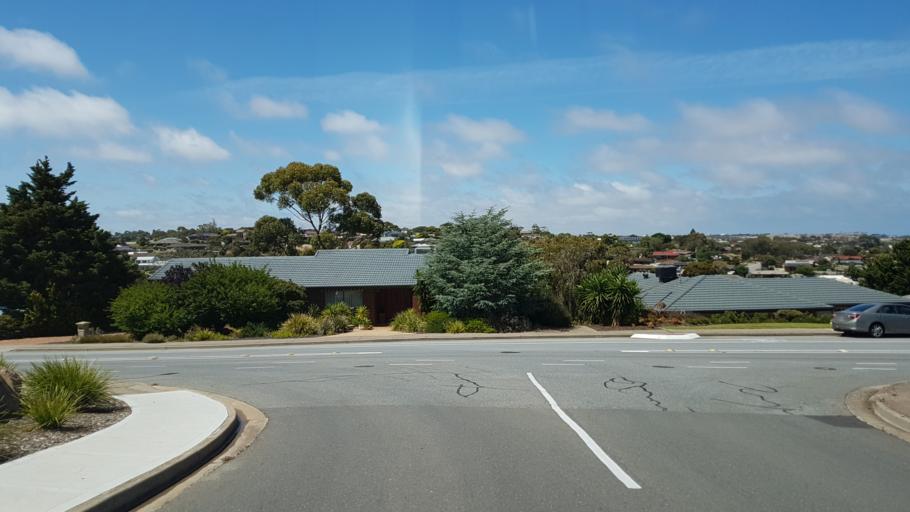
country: AU
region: South Australia
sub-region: Marion
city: Marino
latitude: -35.0694
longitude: 138.5090
